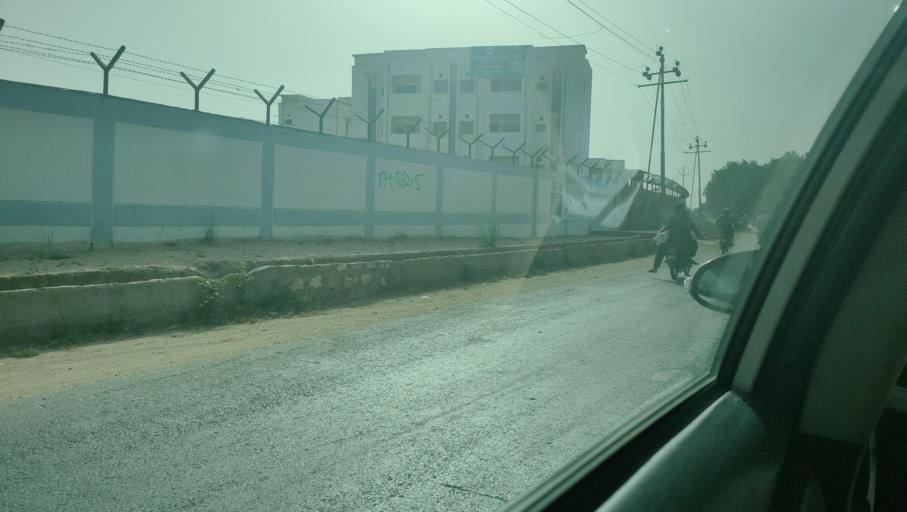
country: PK
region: Sindh
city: Malir Cantonment
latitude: 24.9240
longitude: 67.1816
